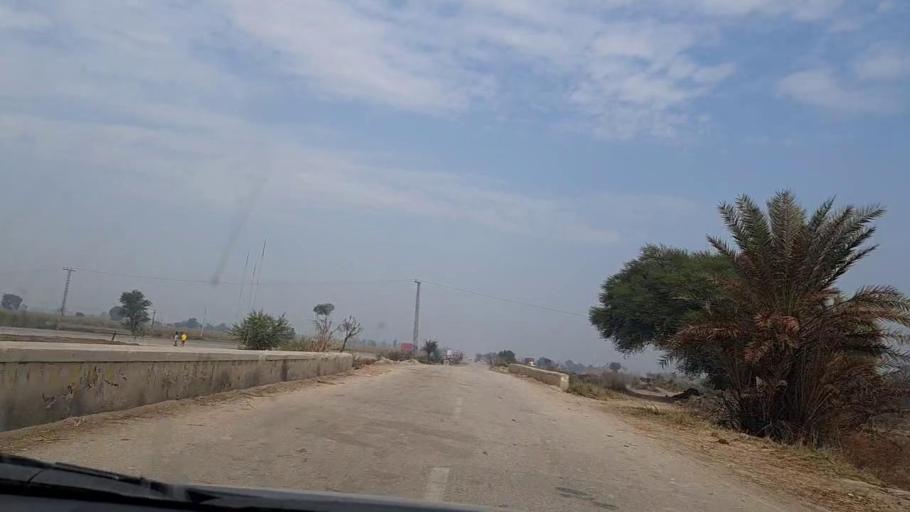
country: PK
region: Sindh
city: Daulatpur
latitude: 26.5256
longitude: 67.9734
